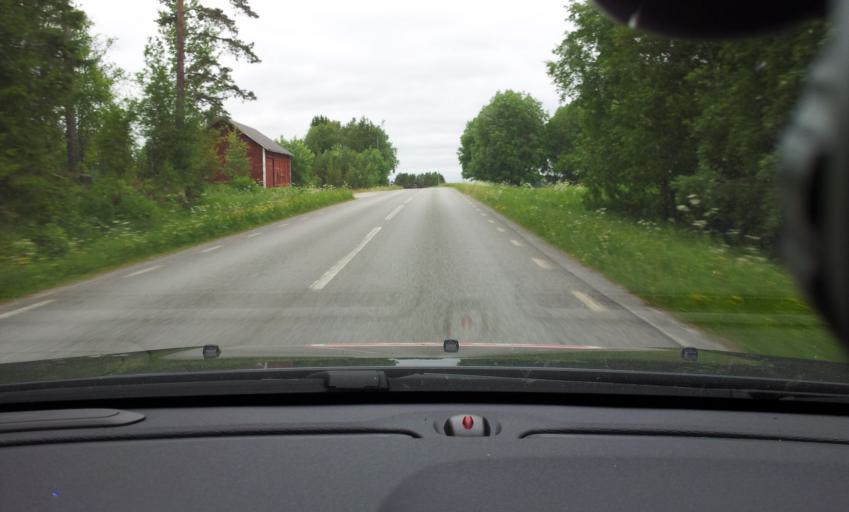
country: SE
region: Jaemtland
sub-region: Krokoms Kommun
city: Krokom
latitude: 63.1364
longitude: 14.1963
